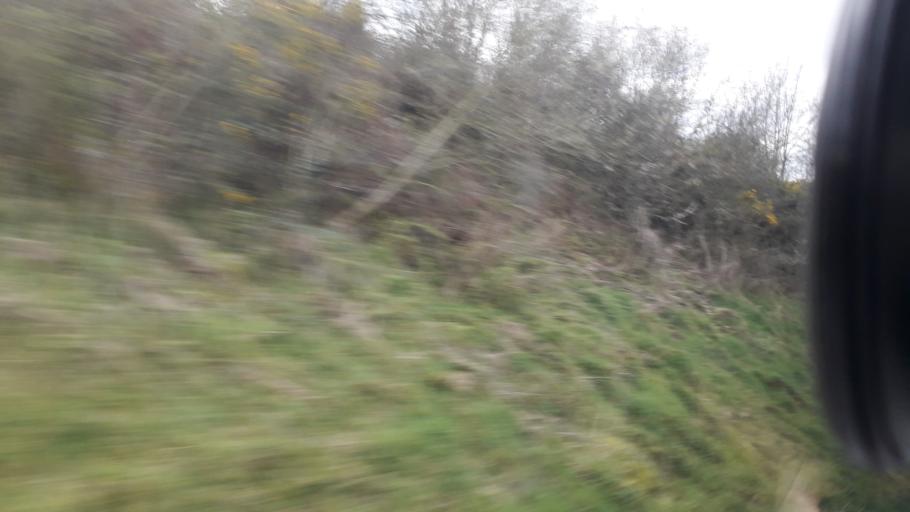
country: IE
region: Leinster
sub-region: An Iarmhi
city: An Muileann gCearr
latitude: 53.6055
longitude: -7.4009
